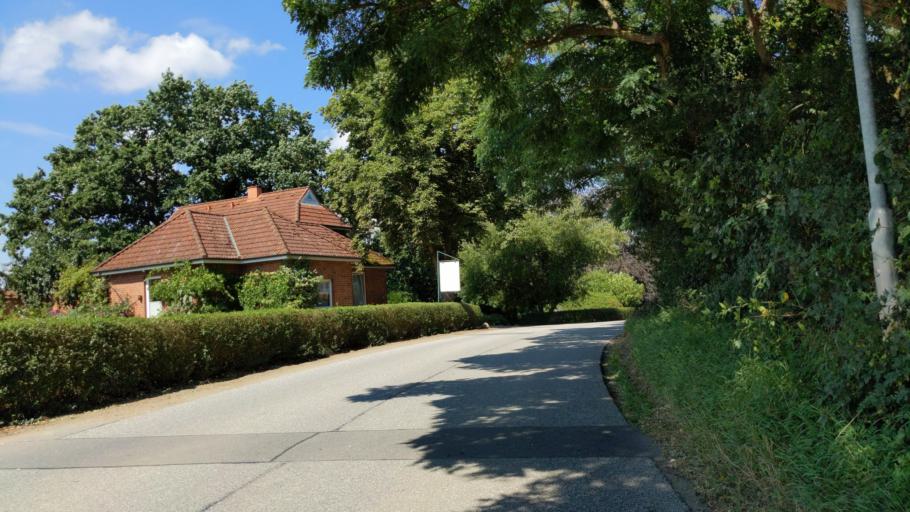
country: DE
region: Schleswig-Holstein
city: Krummesse
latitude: 53.8146
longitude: 10.6774
